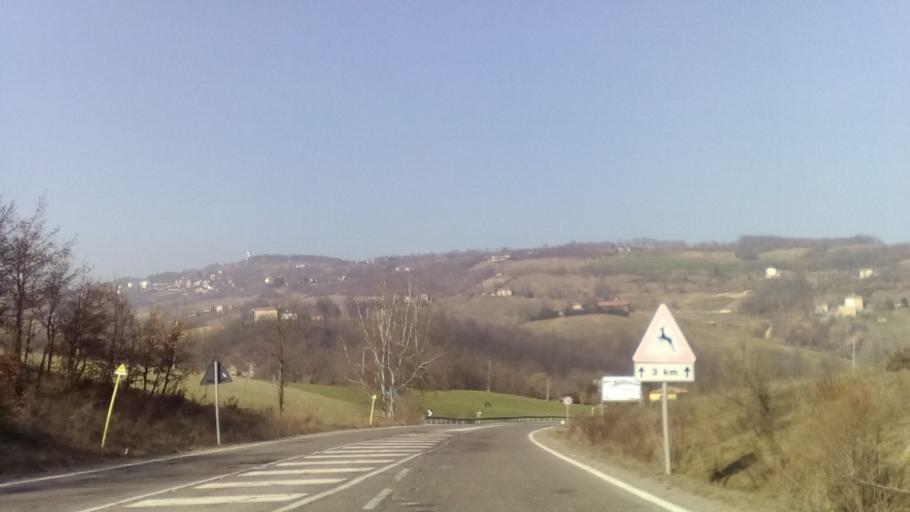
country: IT
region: Emilia-Romagna
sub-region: Provincia di Modena
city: Sant'Antonio
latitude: 44.3989
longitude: 10.8213
